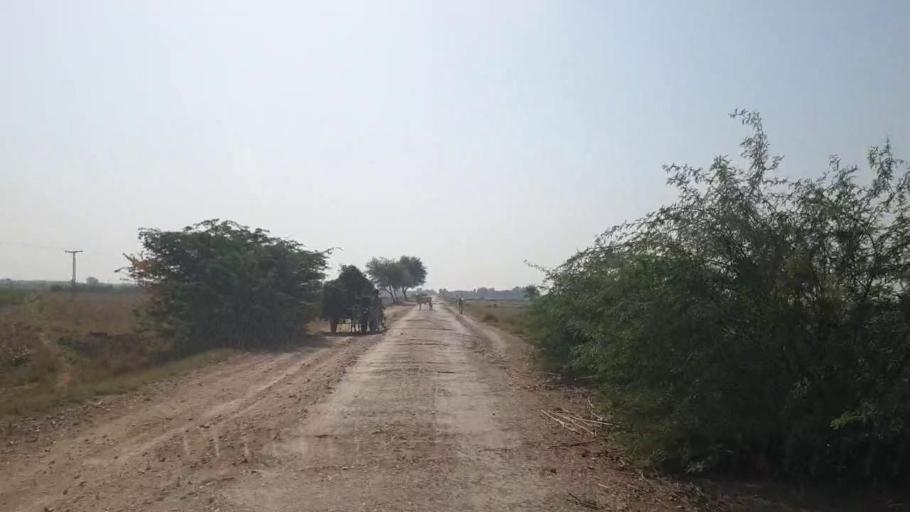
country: PK
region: Sindh
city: Shahdadpur
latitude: 25.9006
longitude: 68.7468
